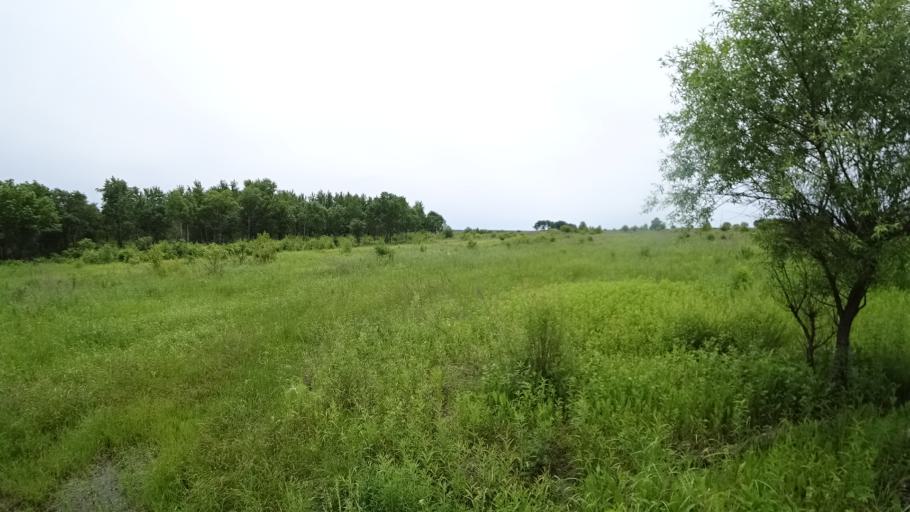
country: RU
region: Primorskiy
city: Arsen'yev
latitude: 44.1822
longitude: 133.3222
